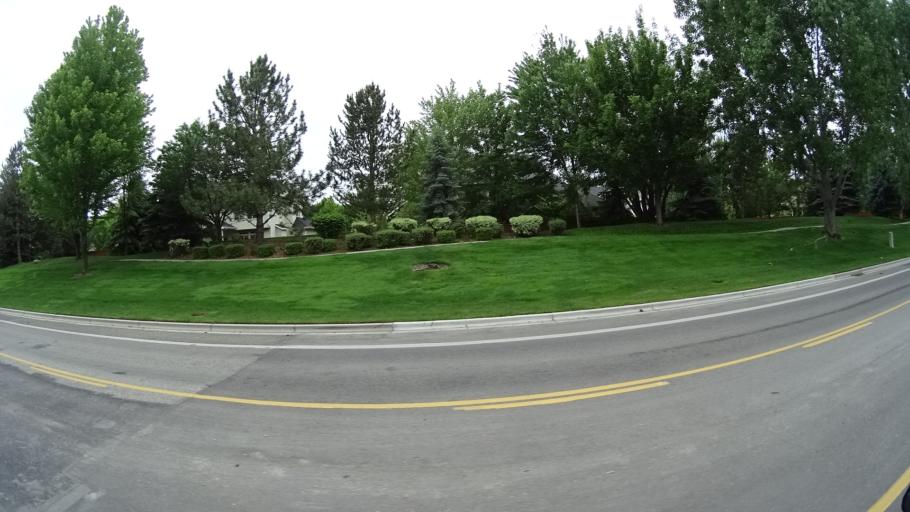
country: US
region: Idaho
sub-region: Ada County
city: Eagle
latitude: 43.7064
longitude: -116.3517
